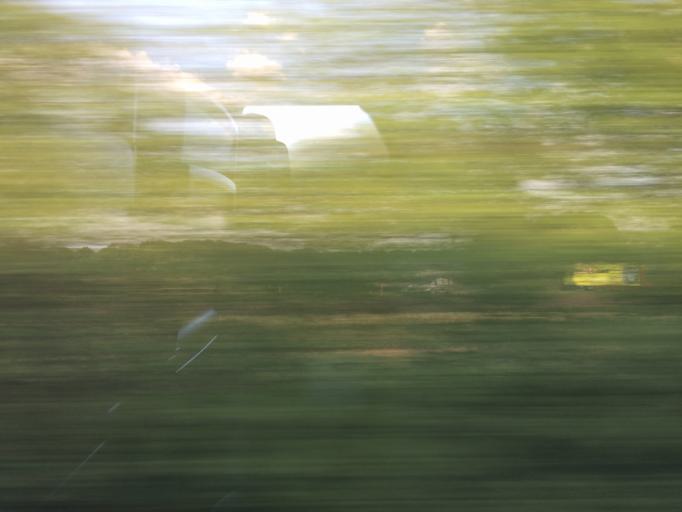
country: DE
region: North Rhine-Westphalia
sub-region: Regierungsbezirk Dusseldorf
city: Hochfeld
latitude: 51.3433
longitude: 6.7806
